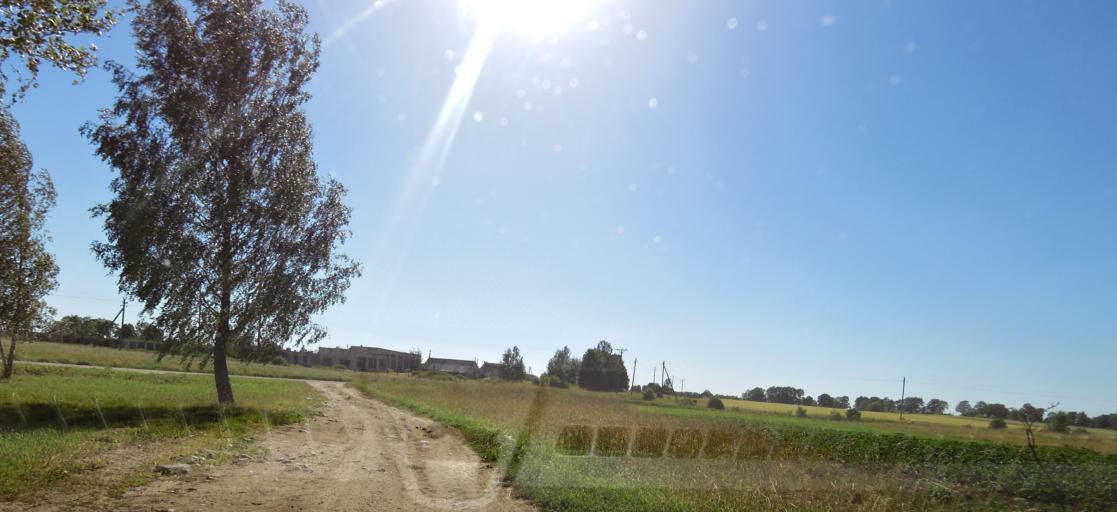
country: LT
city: Vabalninkas
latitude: 56.0270
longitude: 24.6556
